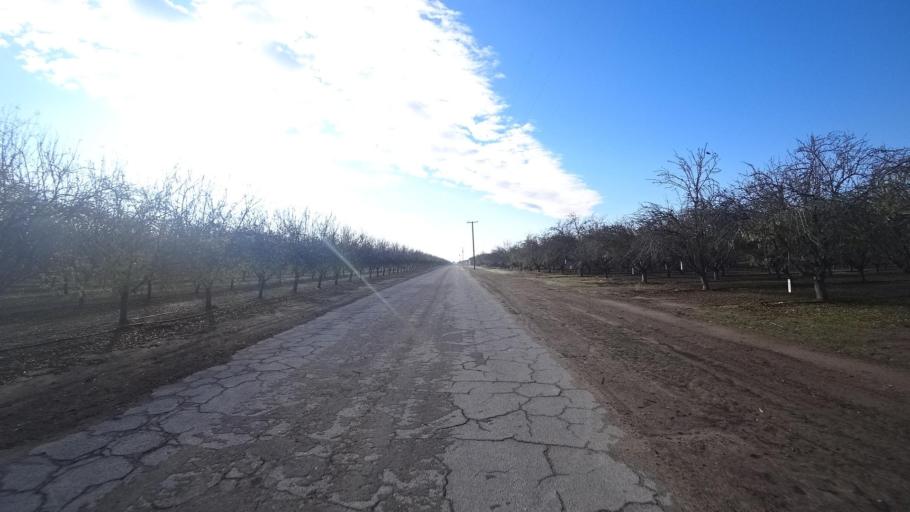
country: US
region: California
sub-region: Kern County
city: Delano
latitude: 35.7140
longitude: -119.3208
